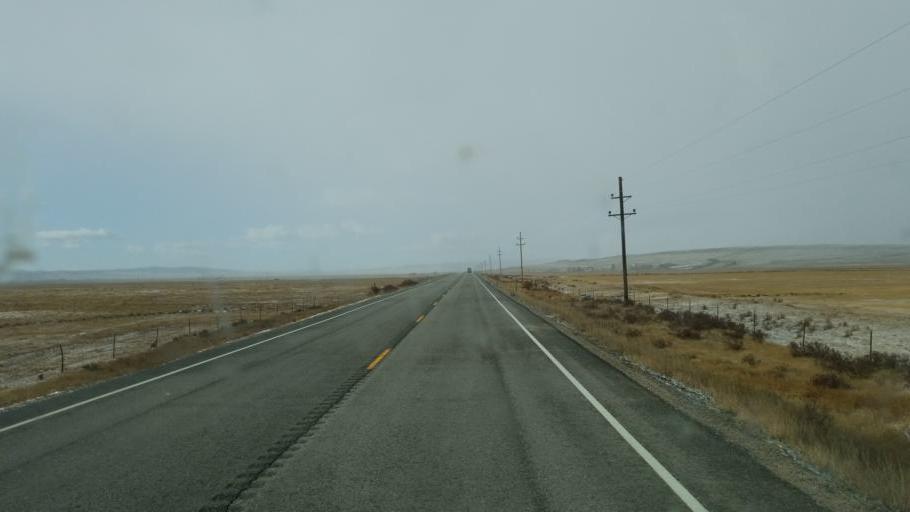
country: US
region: Colorado
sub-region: Summit County
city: Breckenridge
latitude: 39.4008
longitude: -105.7814
